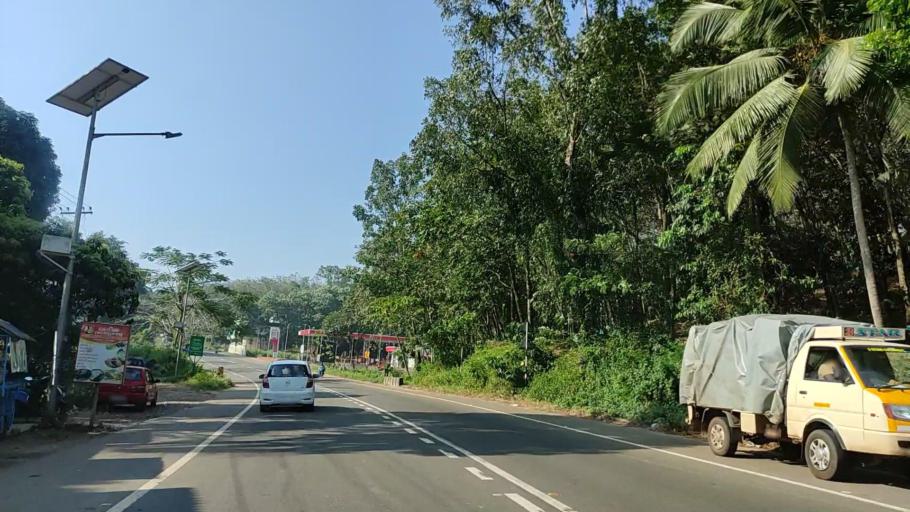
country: IN
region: Kerala
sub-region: Kollam
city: Punalur
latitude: 8.9175
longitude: 76.8543
